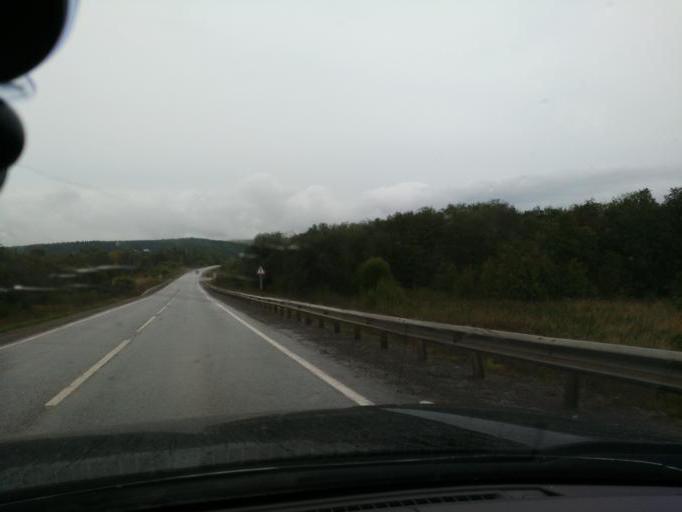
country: RU
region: Perm
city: Yugo-Kamskiy
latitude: 57.7108
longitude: 55.6352
